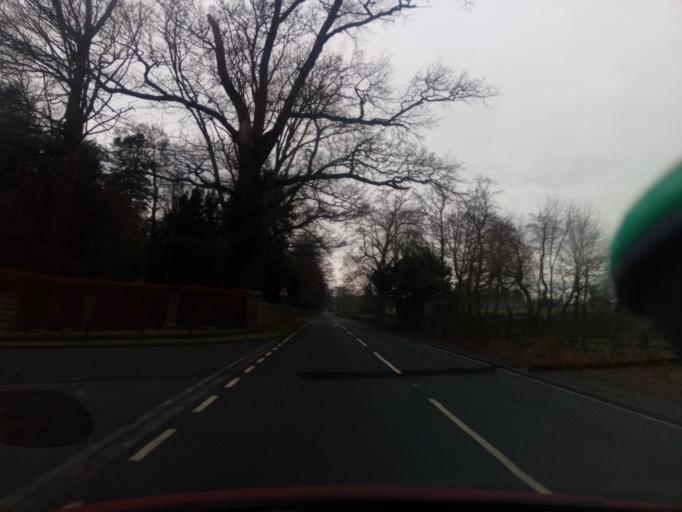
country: GB
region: England
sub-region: Northumberland
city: Wall
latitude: 55.0287
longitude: -2.1402
